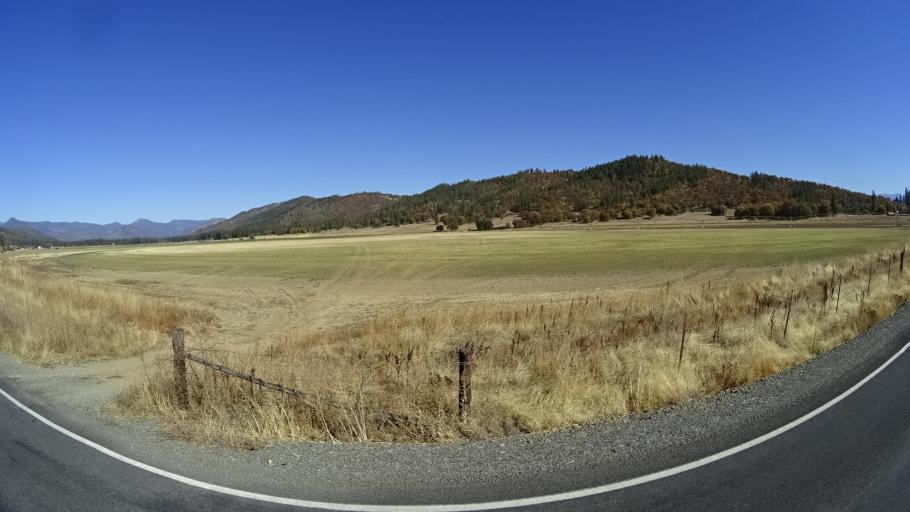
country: US
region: California
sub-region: Siskiyou County
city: Yreka
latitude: 41.5583
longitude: -122.9232
